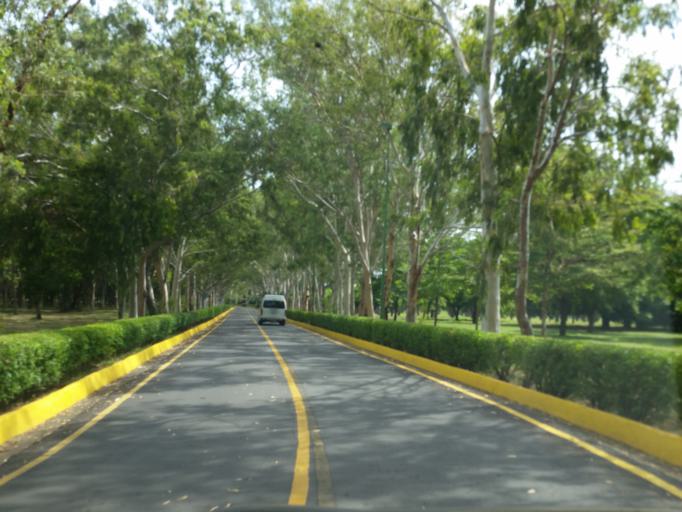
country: NI
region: Managua
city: Masachapa
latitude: 11.8023
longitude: -86.5173
